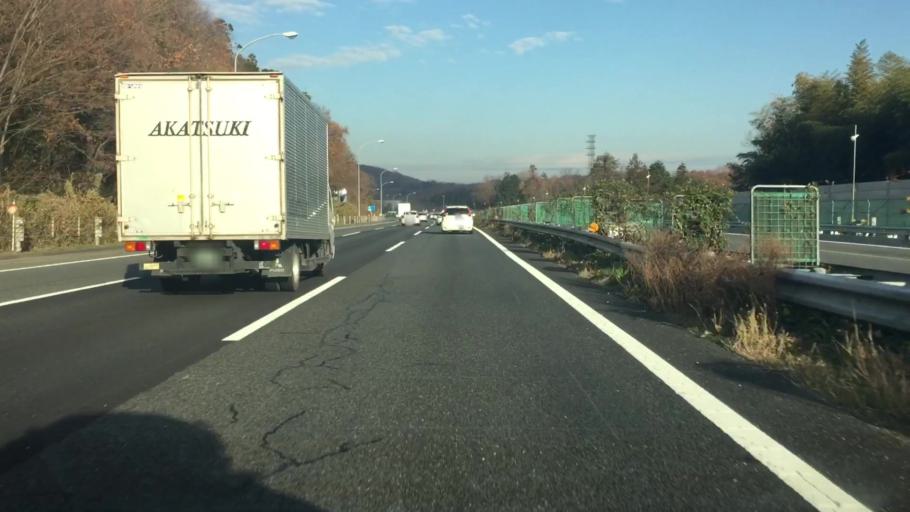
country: JP
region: Saitama
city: Ogawa
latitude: 36.0783
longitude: 139.3000
